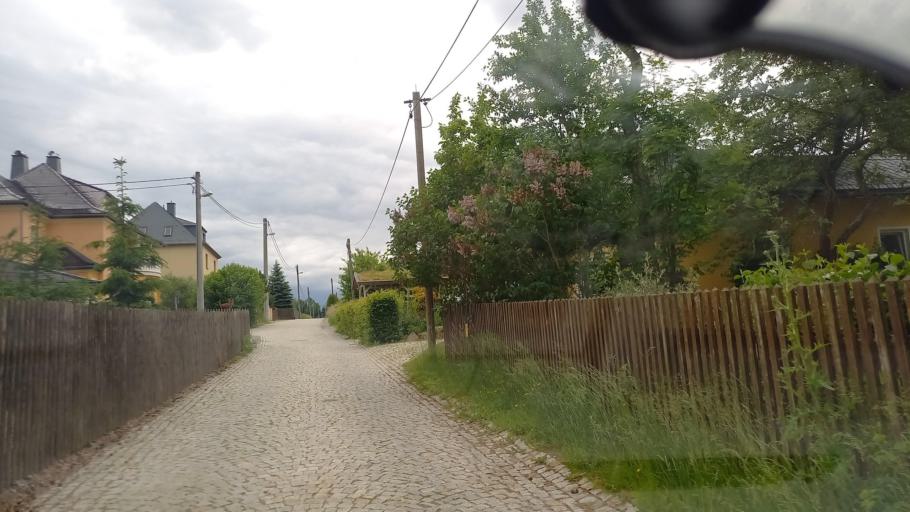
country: DE
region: Saxony
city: Kirchberg
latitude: 50.6181
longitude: 12.5284
